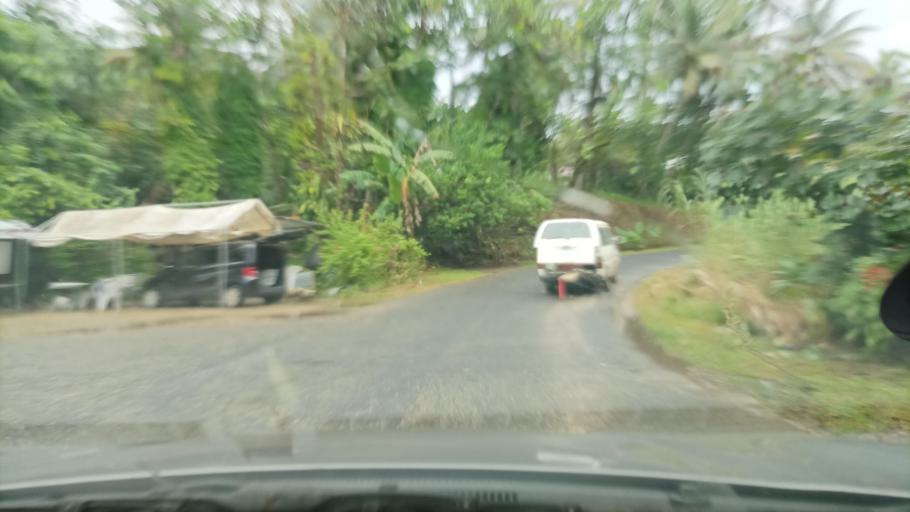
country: FM
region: Pohnpei
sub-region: Sokehs Municipality
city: Palikir - National Government Center
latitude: 6.8385
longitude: 158.1546
